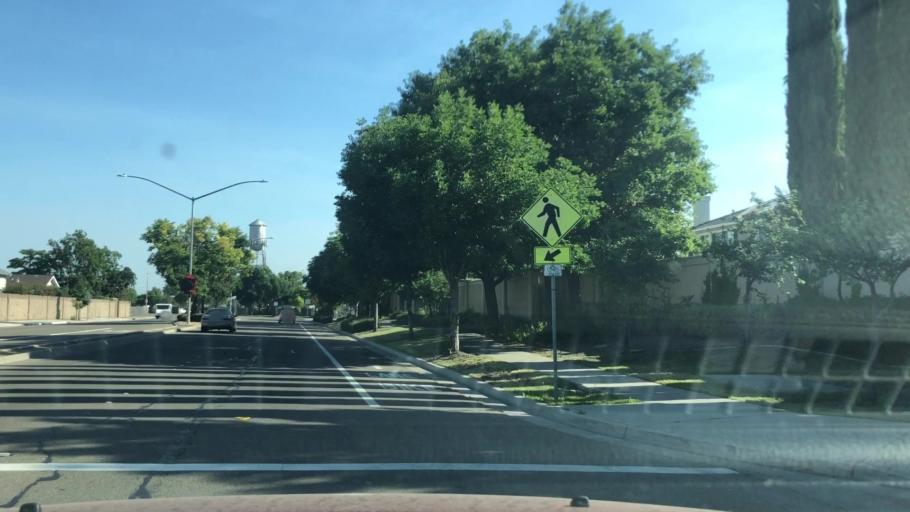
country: US
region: California
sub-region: San Joaquin County
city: Tracy
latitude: 37.7337
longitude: -121.4347
